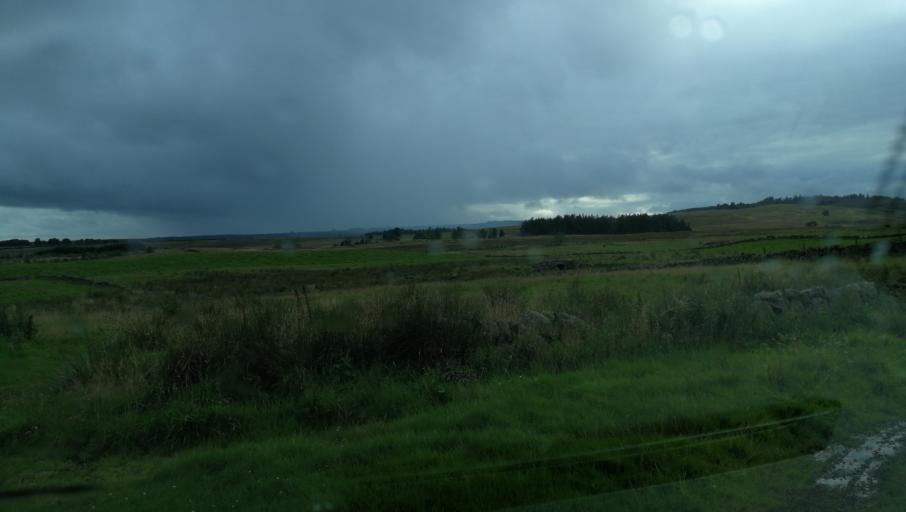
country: GB
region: Scotland
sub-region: Perth and Kinross
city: Blairgowrie
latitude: 56.6676
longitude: -3.3478
